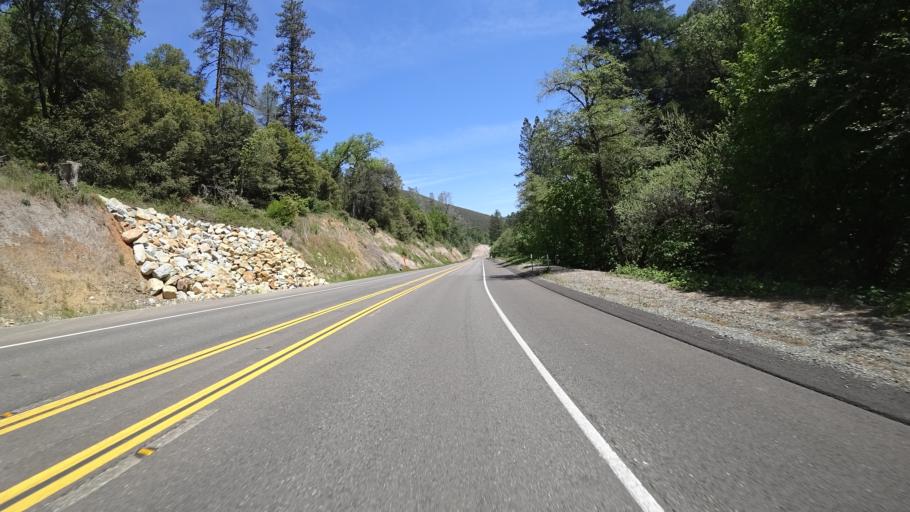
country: US
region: California
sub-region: Trinity County
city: Lewiston
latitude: 40.6738
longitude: -122.6713
